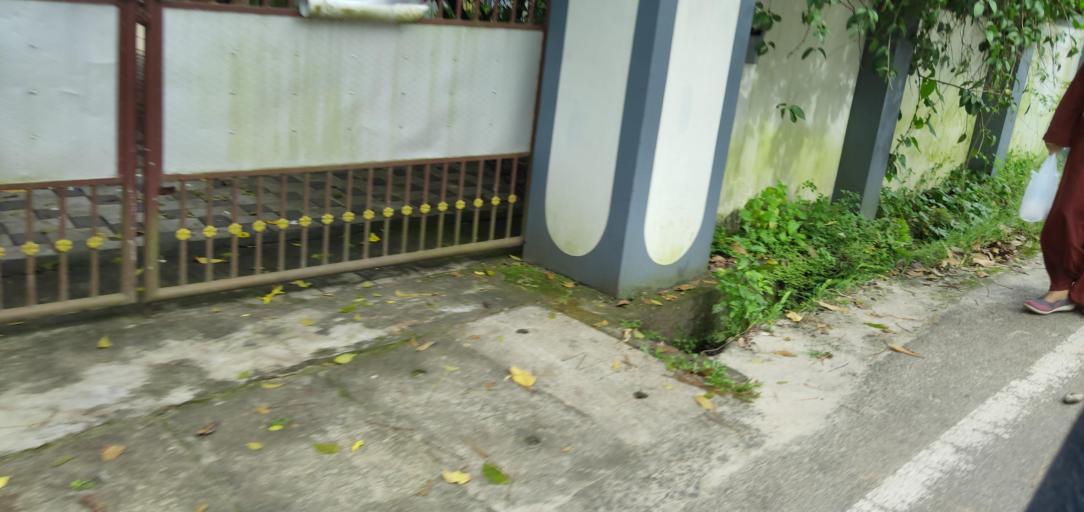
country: IN
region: Kerala
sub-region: Alappuzha
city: Kayankulam
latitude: 9.2164
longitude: 76.4615
